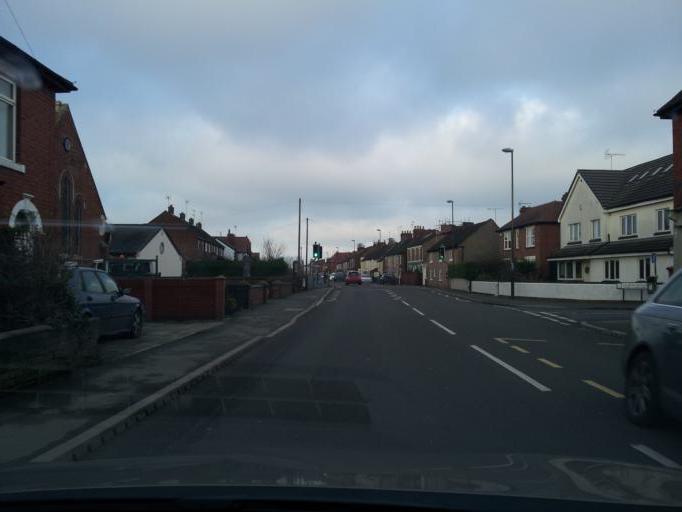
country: GB
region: England
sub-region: Staffordshire
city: Burton upon Trent
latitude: 52.8670
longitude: -1.6807
